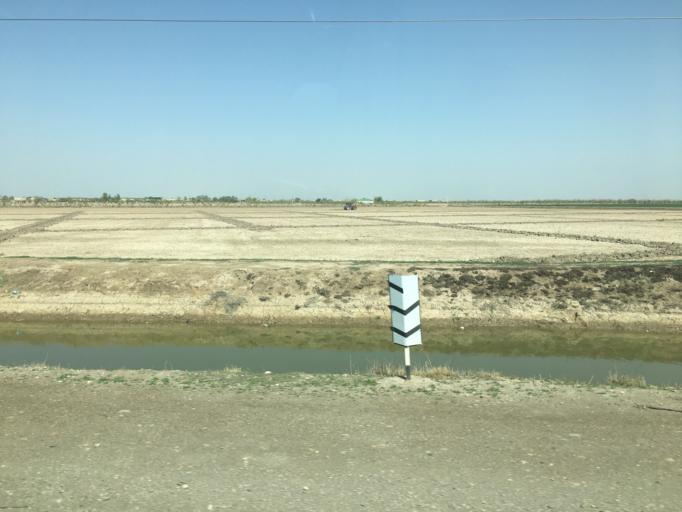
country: TM
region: Lebap
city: Turkmenabat
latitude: 38.9827
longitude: 63.6396
